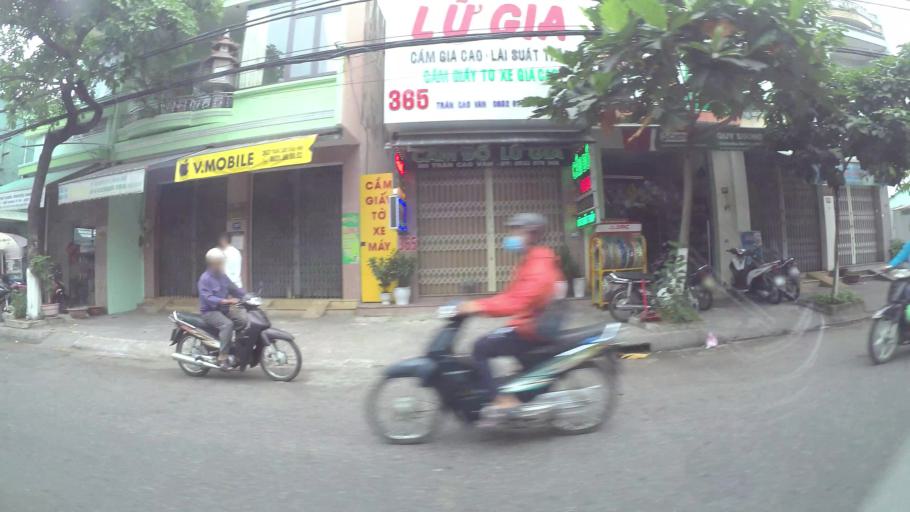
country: VN
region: Da Nang
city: Thanh Khe
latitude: 16.0711
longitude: 108.1962
